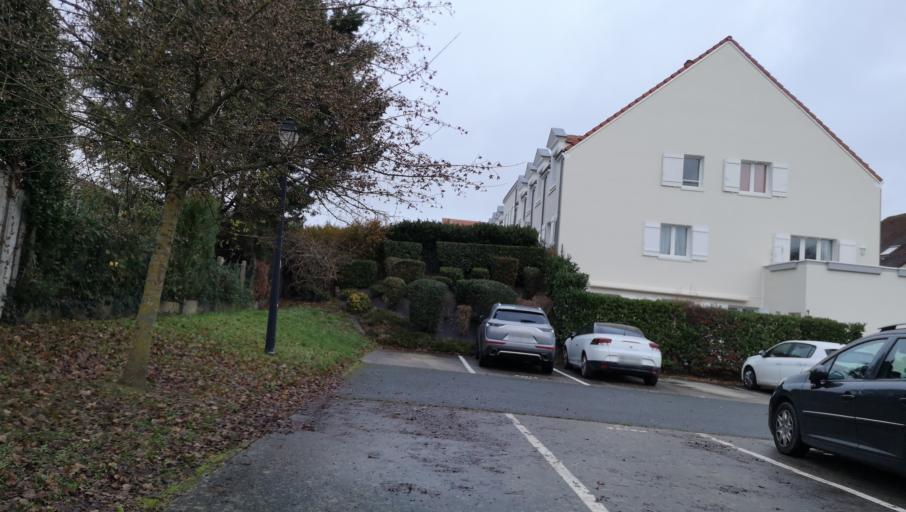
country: FR
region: Centre
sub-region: Departement du Loiret
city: Saint-Jean-de-Braye
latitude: 47.9059
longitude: 1.9618
